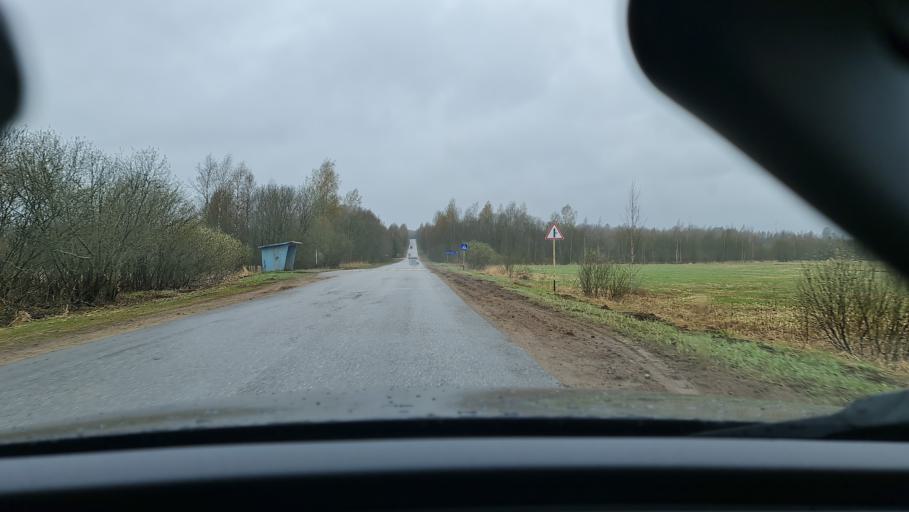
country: RU
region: Novgorod
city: Kresttsy
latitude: 57.9742
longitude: 32.7299
